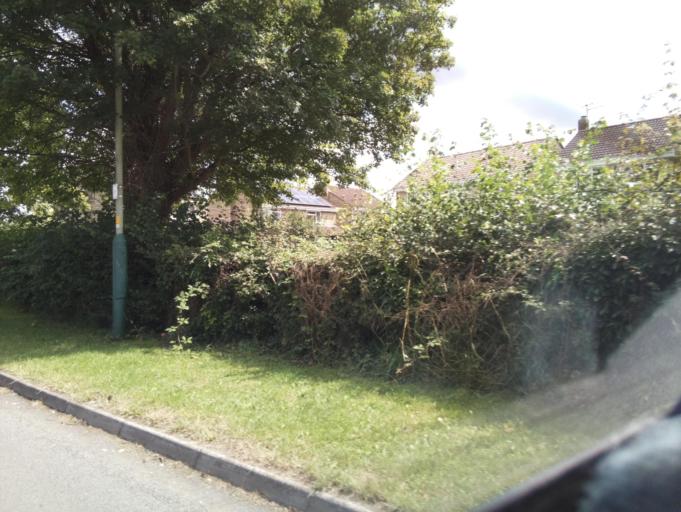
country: GB
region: England
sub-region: Wiltshire
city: Lydiard Tregoze
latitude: 51.5511
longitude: -1.8352
